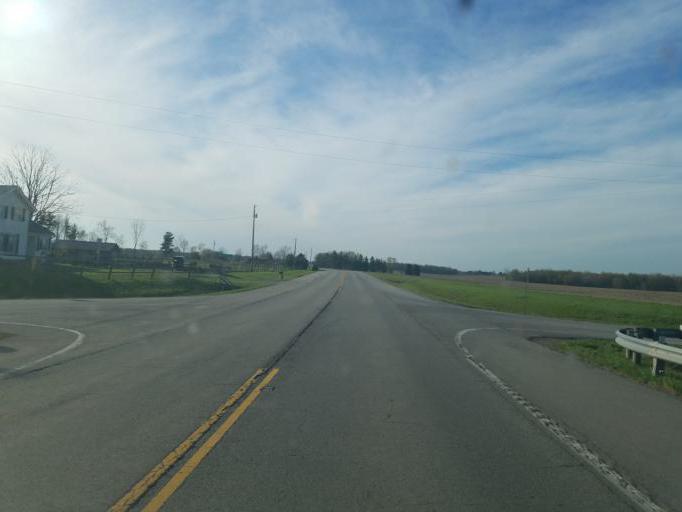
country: US
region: Ohio
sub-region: Huron County
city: New London
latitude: 41.0672
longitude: -82.4534
